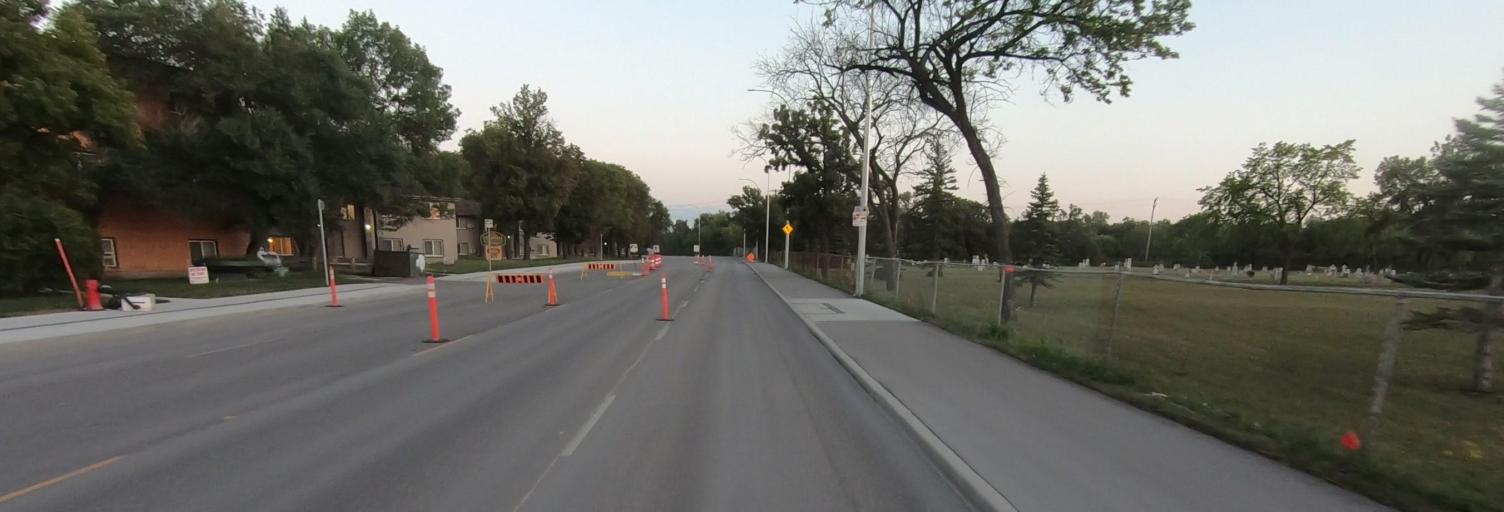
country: CA
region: Manitoba
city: Winnipeg
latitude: 49.8687
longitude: -97.0922
